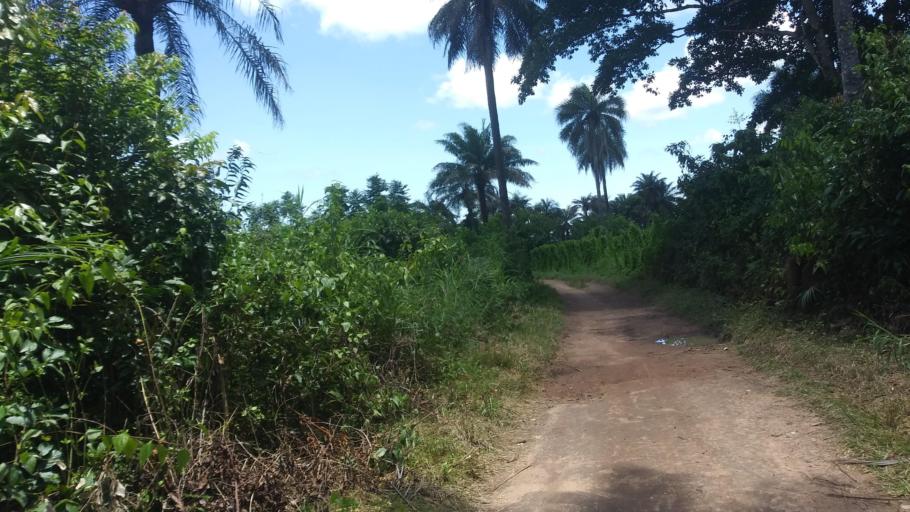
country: SL
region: Northern Province
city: Makeni
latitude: 8.8975
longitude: -11.9977
